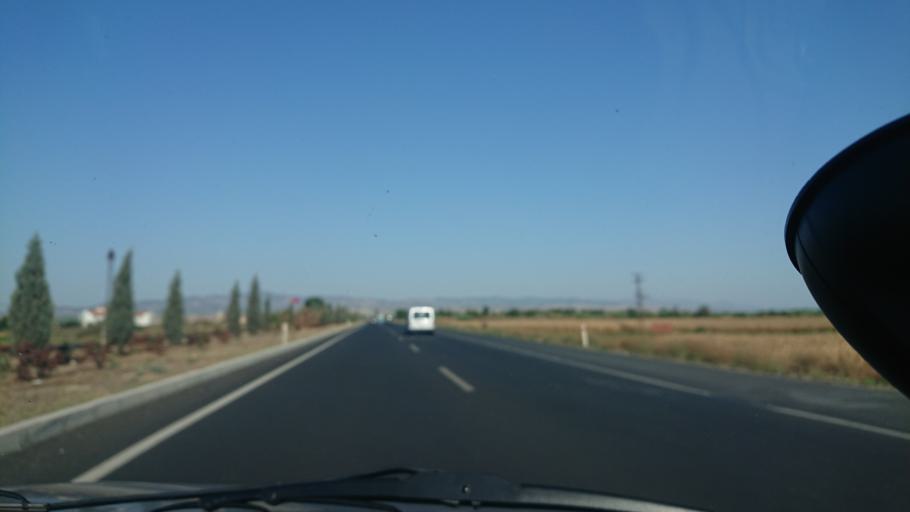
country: TR
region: Manisa
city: Adala
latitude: 38.5061
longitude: 28.2309
